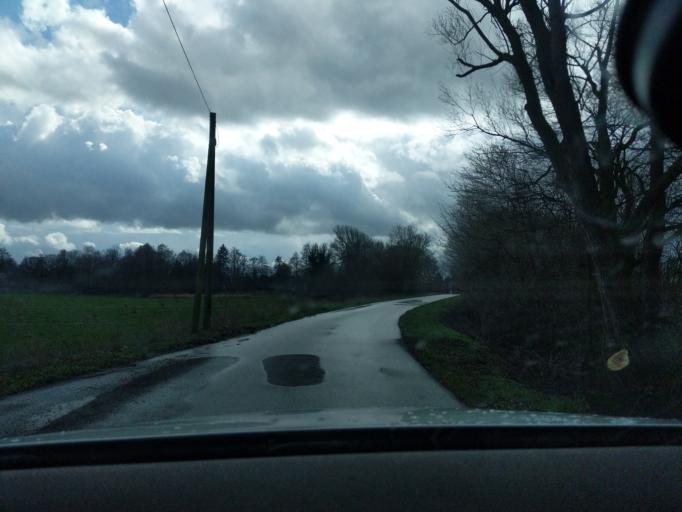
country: DE
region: Lower Saxony
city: Kranenburg
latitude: 53.6136
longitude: 9.2033
